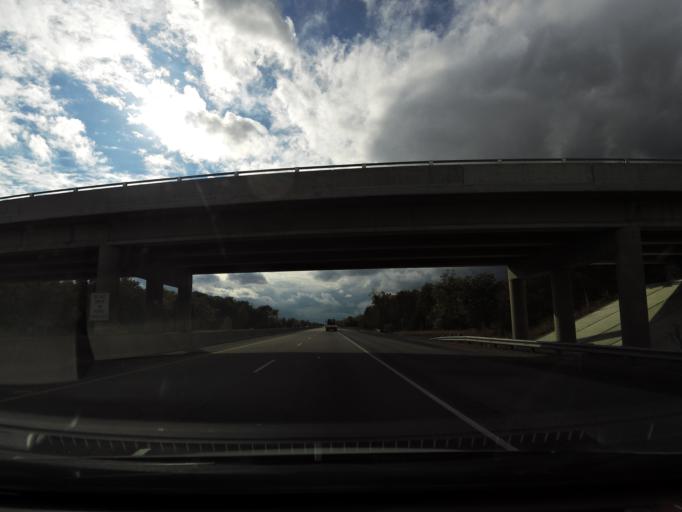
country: CA
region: Ontario
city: Belleville
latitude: 44.2200
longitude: -77.2991
